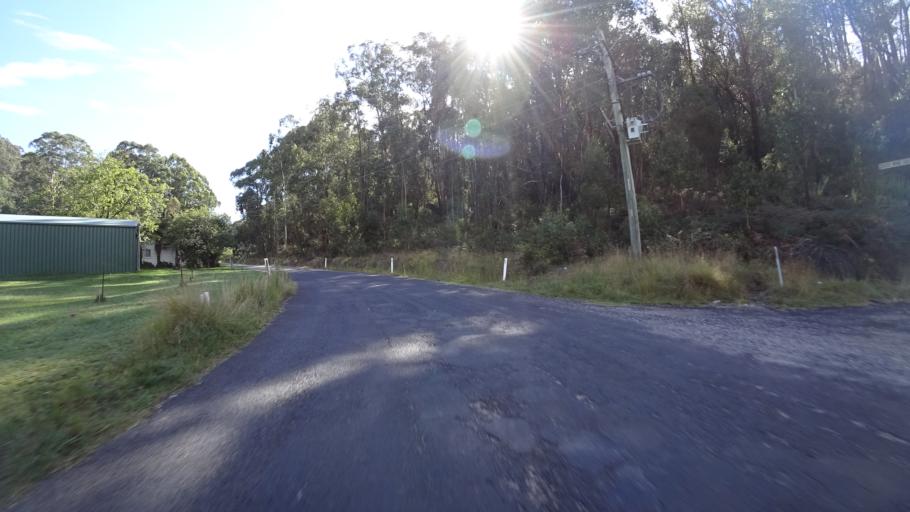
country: AU
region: New South Wales
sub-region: Lithgow
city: Lithgow
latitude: -33.4585
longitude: 150.1712
